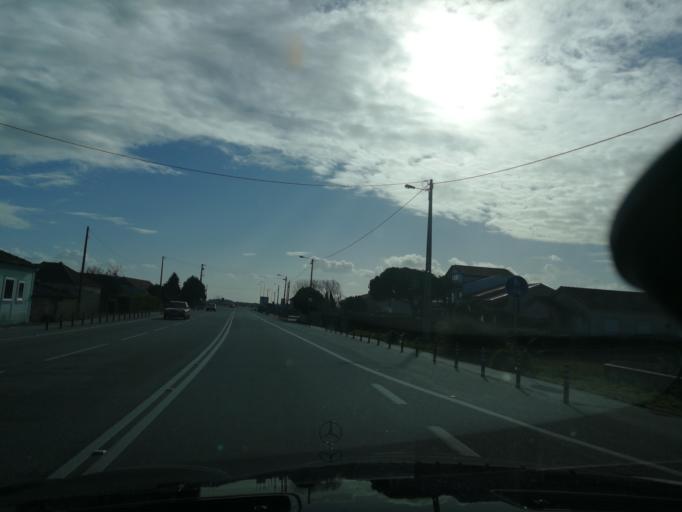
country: PT
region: Aveiro
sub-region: Murtosa
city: Murtosa
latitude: 40.7702
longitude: -8.6951
